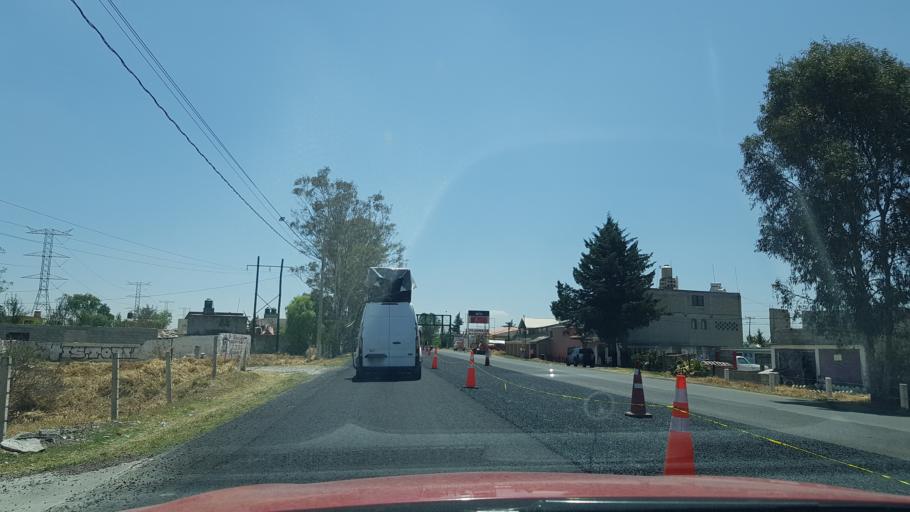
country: MX
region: Mexico
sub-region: Ixtlahuaca
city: Santo Domingo de Guzman
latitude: 19.5975
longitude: -99.7726
